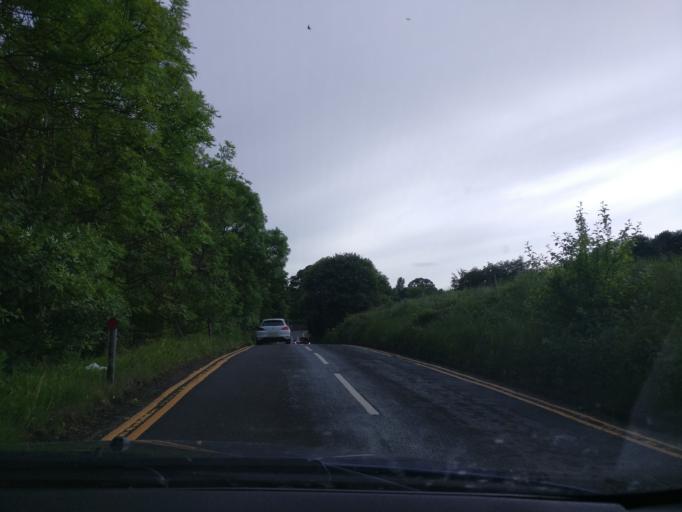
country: GB
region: Scotland
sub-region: West Lothian
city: Seafield
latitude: 55.9221
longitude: -3.1413
